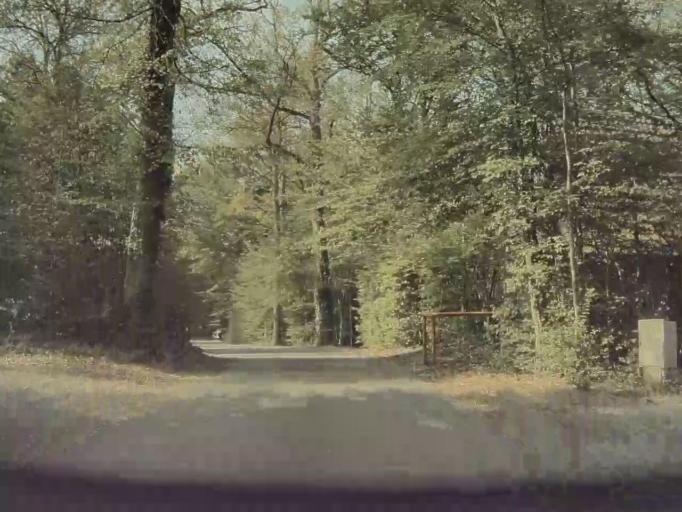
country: BE
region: Wallonia
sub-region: Province du Luxembourg
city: Durbuy
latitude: 50.3462
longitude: 5.4284
